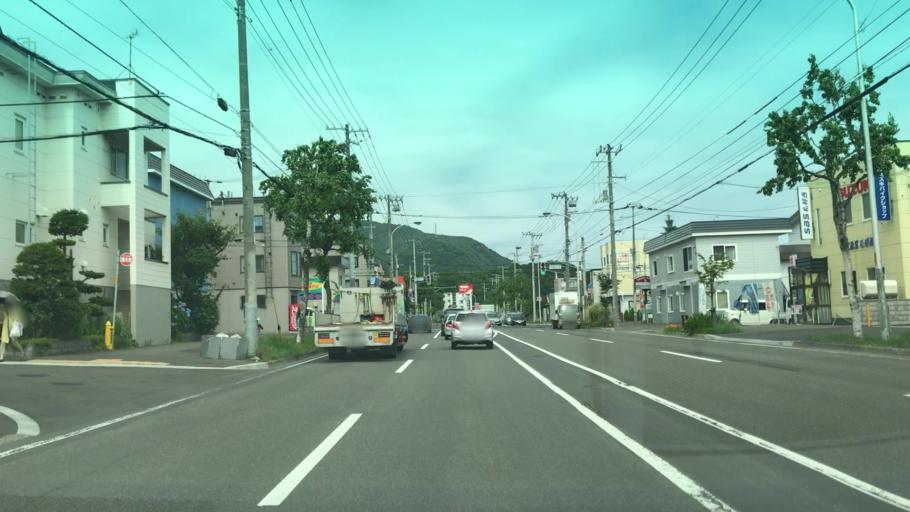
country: JP
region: Hokkaido
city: Sapporo
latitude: 43.0765
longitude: 141.2745
